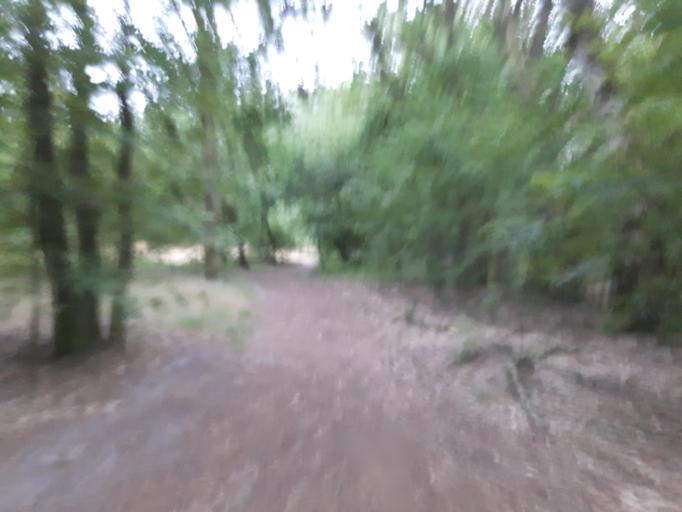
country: DE
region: Lower Saxony
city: Delmenhorst
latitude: 53.0157
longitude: 8.6850
